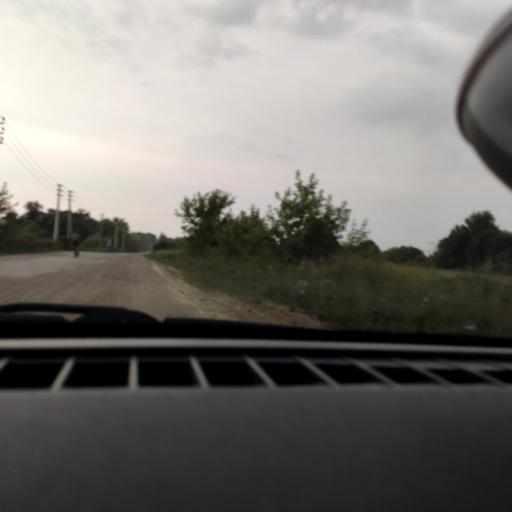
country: RU
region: Perm
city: Kondratovo
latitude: 57.9969
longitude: 55.9984
